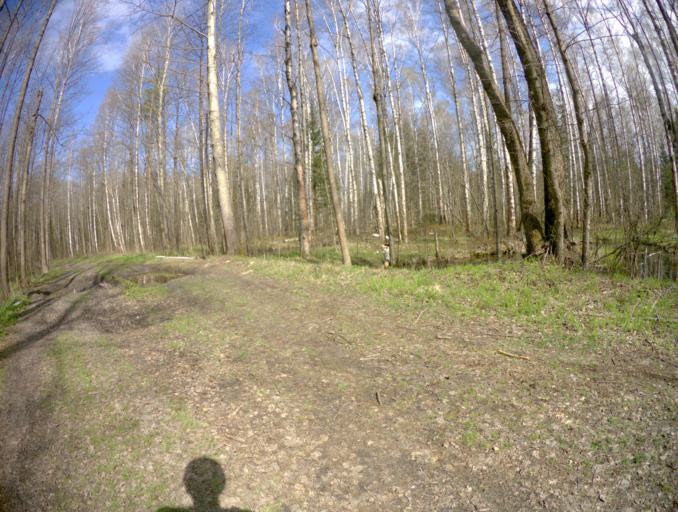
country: RU
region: Vladimir
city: Mezinovskiy
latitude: 55.5124
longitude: 40.2900
